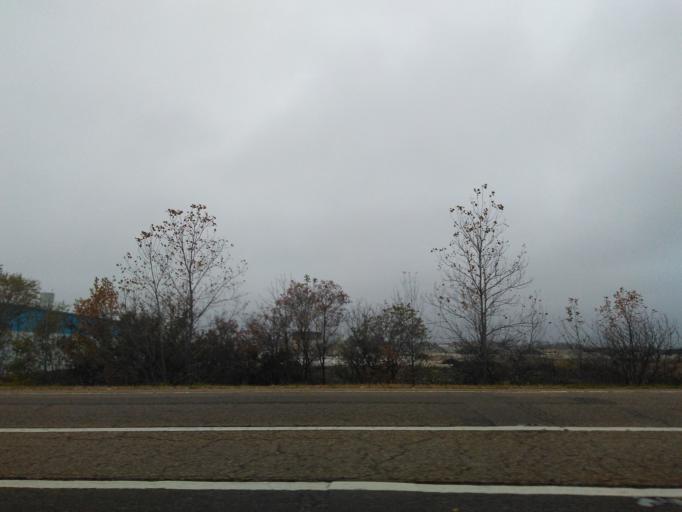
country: US
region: Illinois
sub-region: Madison County
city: Troy
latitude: 38.7465
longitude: -89.9096
